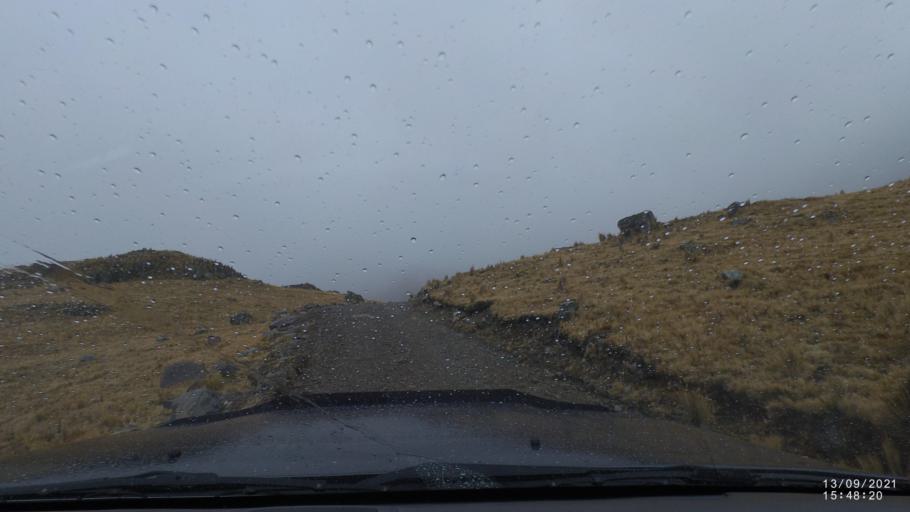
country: BO
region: Cochabamba
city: Colomi
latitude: -17.3111
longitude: -65.7162
